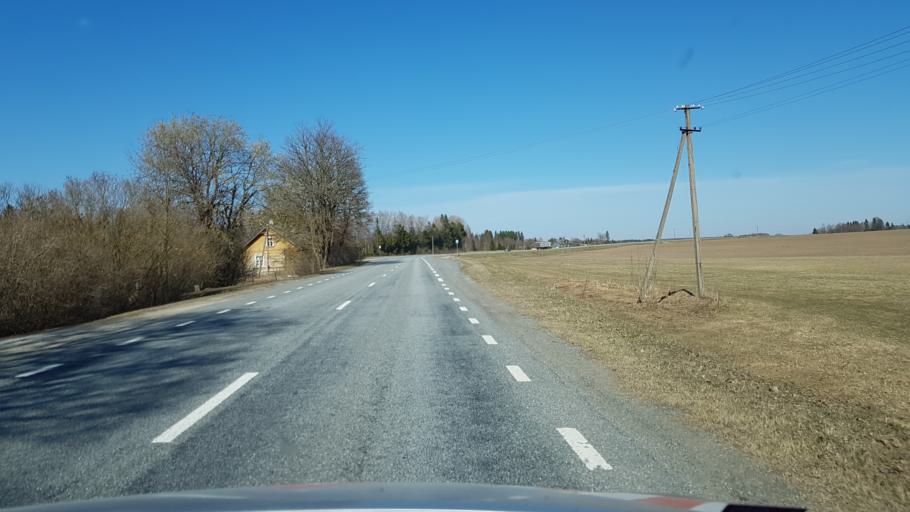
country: EE
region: Jaervamaa
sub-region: Jaerva-Jaani vald
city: Jarva-Jaani
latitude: 59.0670
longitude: 25.9327
